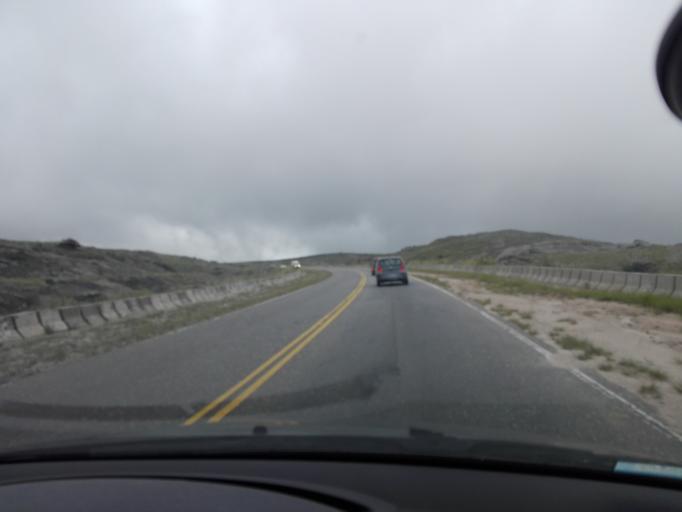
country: AR
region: Cordoba
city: Cuesta Blanca
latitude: -31.6120
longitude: -64.7479
